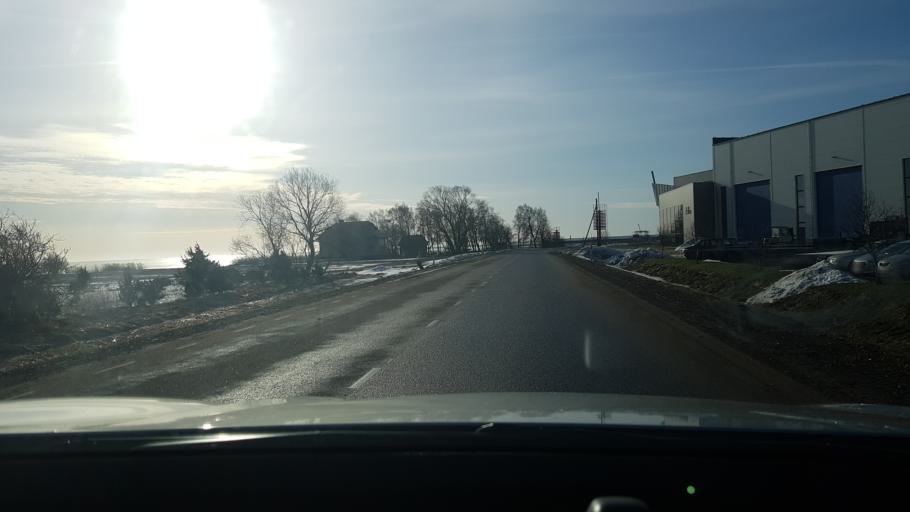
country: EE
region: Saare
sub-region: Kuressaare linn
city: Kuressaare
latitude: 58.2217
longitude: 22.5068
